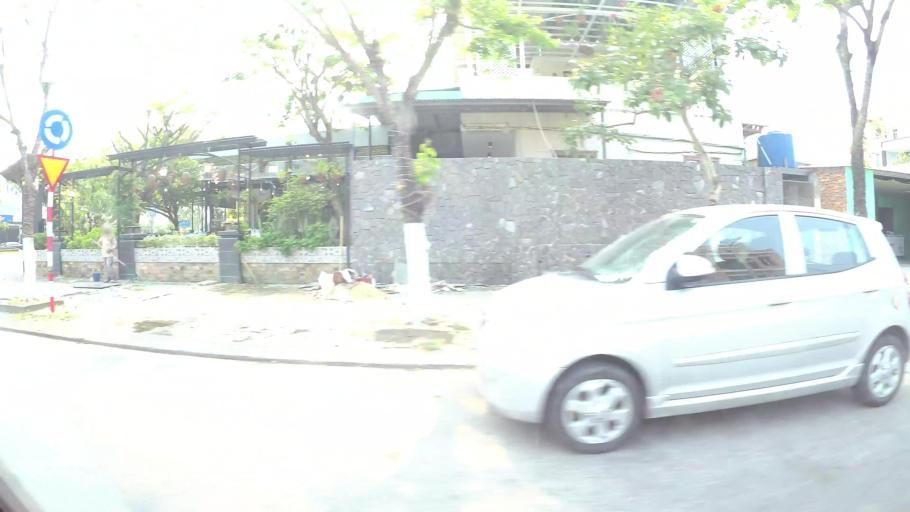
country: VN
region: Da Nang
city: Cam Le
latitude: 16.0404
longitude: 108.2137
